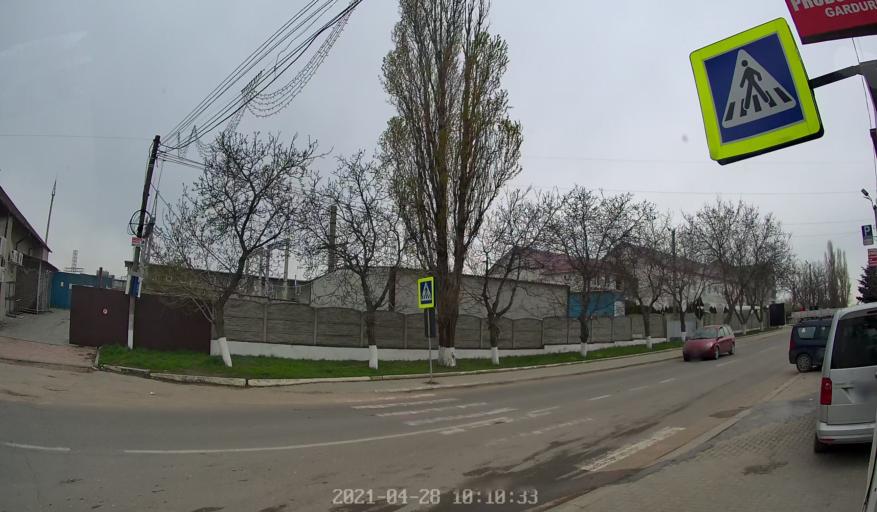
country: MD
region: Chisinau
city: Chisinau
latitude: 46.9844
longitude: 28.9310
